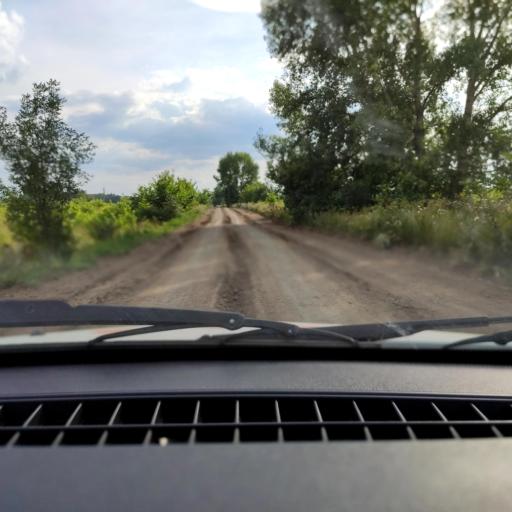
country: RU
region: Bashkortostan
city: Blagoveshchensk
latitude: 54.9284
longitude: 55.9508
